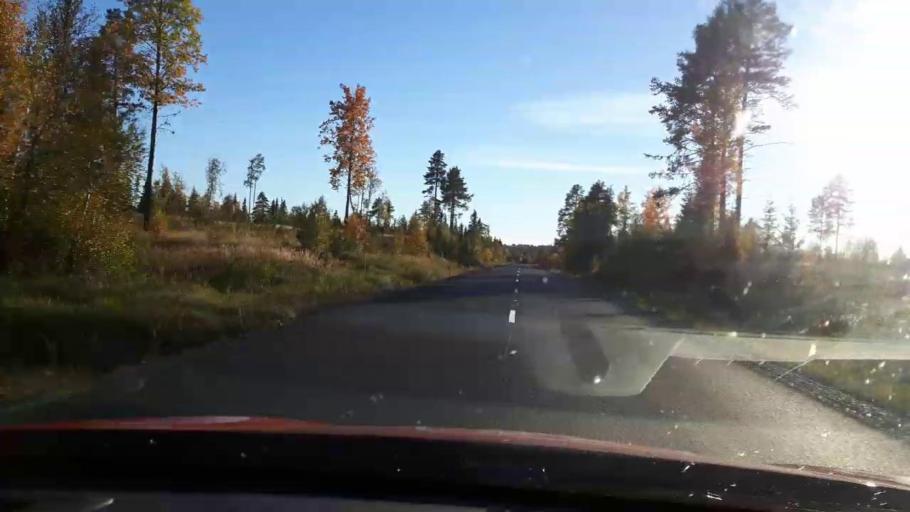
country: SE
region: Jaemtland
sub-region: OEstersunds Kommun
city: Lit
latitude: 63.5545
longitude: 14.8926
